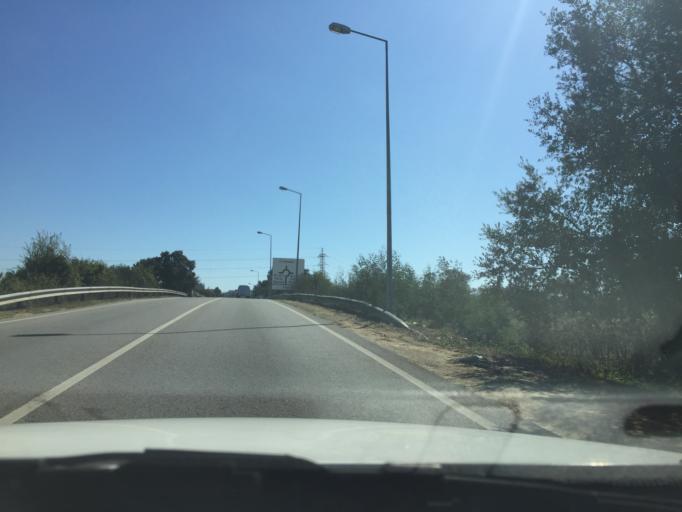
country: PT
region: Aveiro
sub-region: Anadia
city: Arcos
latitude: 40.4446
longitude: -8.4571
